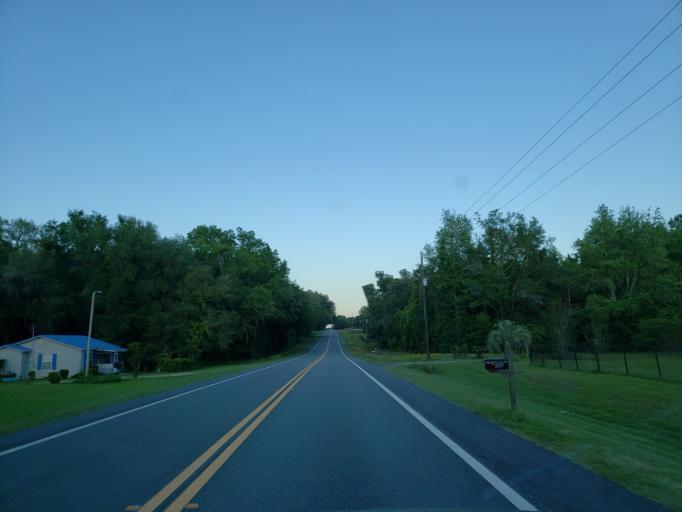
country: US
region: Georgia
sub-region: Echols County
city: Statenville
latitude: 30.5813
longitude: -83.2148
